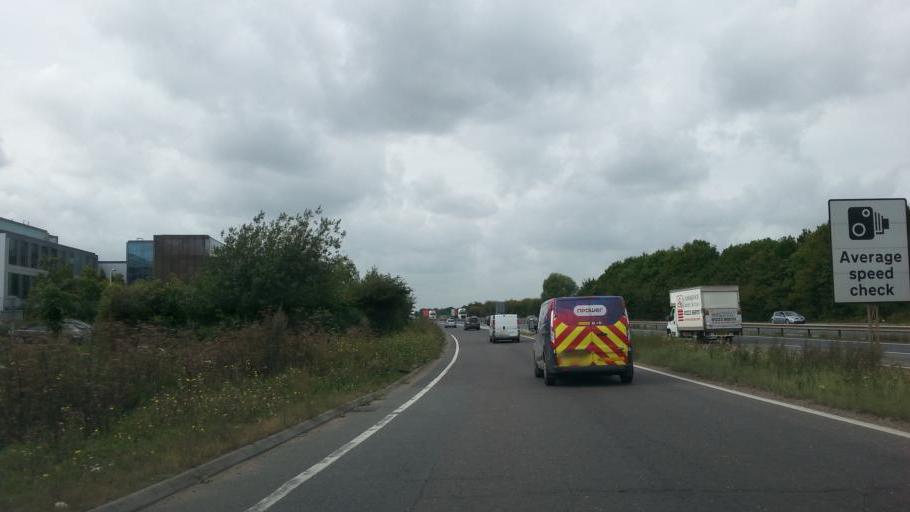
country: GB
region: England
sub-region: Cambridgeshire
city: Histon
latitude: 52.2378
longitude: 0.1473
